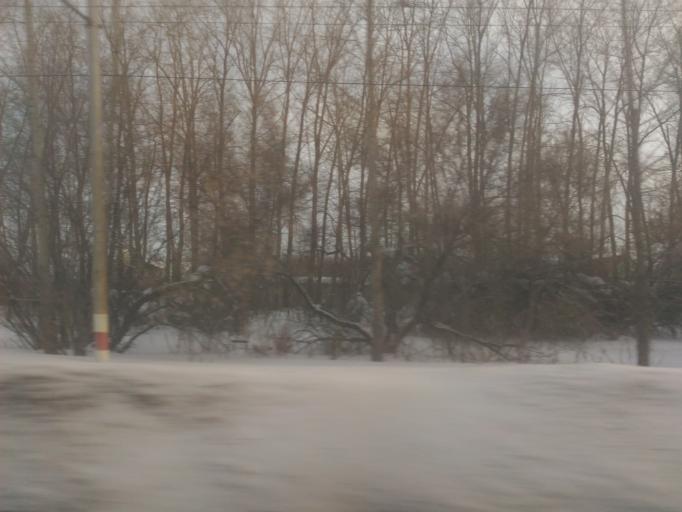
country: RU
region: Ulyanovsk
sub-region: Ulyanovskiy Rayon
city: Ulyanovsk
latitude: 54.3611
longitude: 48.3425
